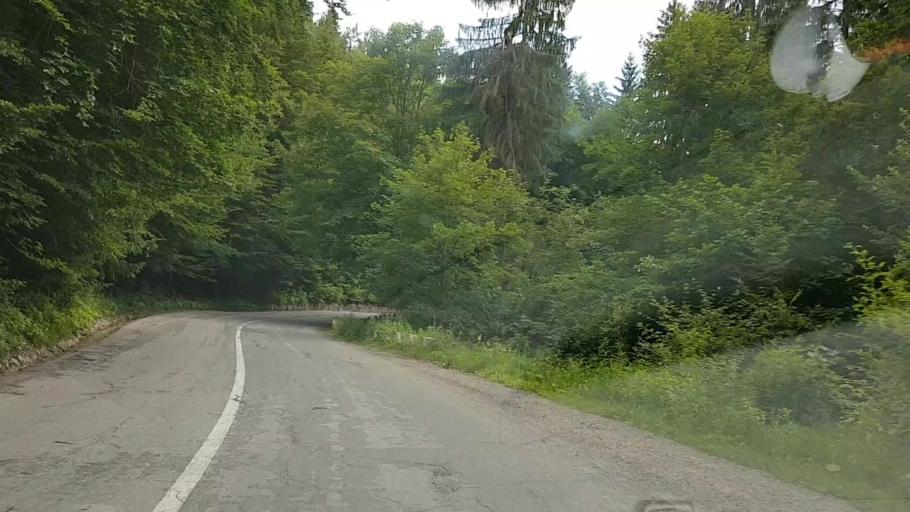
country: RO
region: Neamt
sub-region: Comuna Pangarati
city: Pangarati
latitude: 46.9875
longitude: 26.1176
